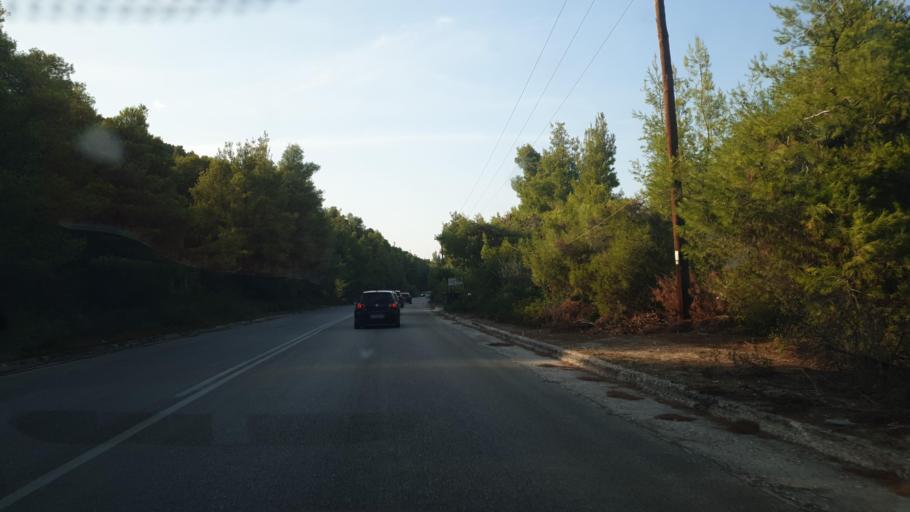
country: GR
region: Central Macedonia
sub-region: Nomos Chalkidikis
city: Agios Nikolaos
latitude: 40.2019
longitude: 23.7633
